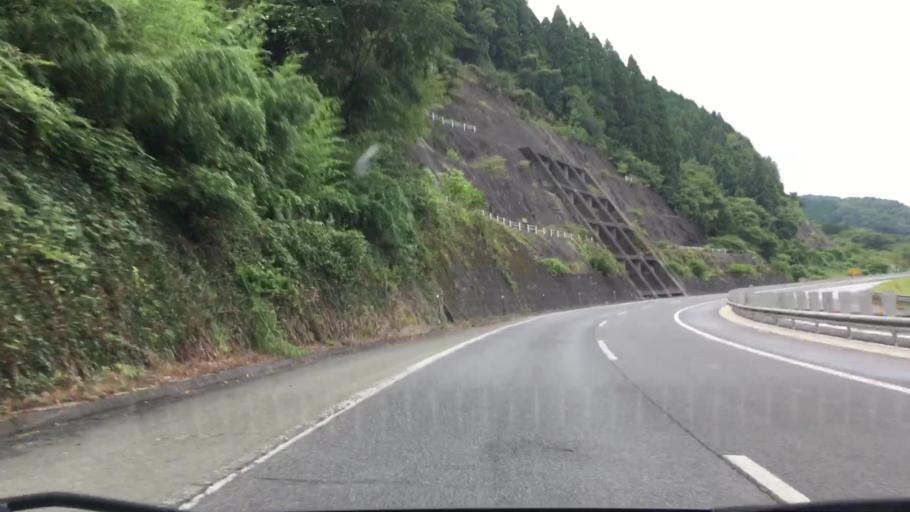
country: JP
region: Hiroshima
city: Shobara
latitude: 34.8972
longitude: 133.2362
